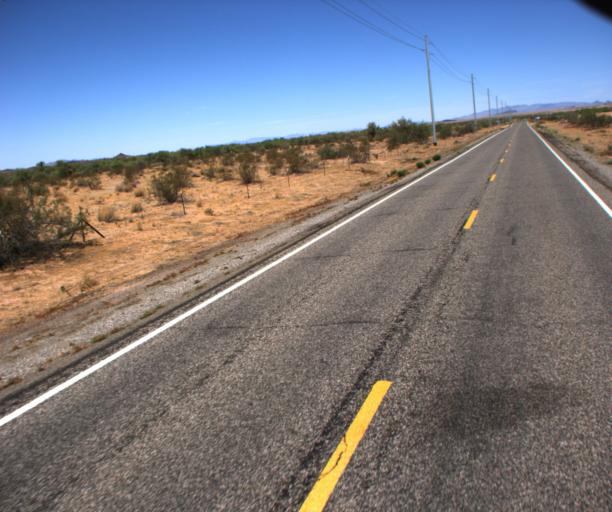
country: US
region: Arizona
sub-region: La Paz County
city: Cienega Springs
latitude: 33.9652
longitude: -114.0364
